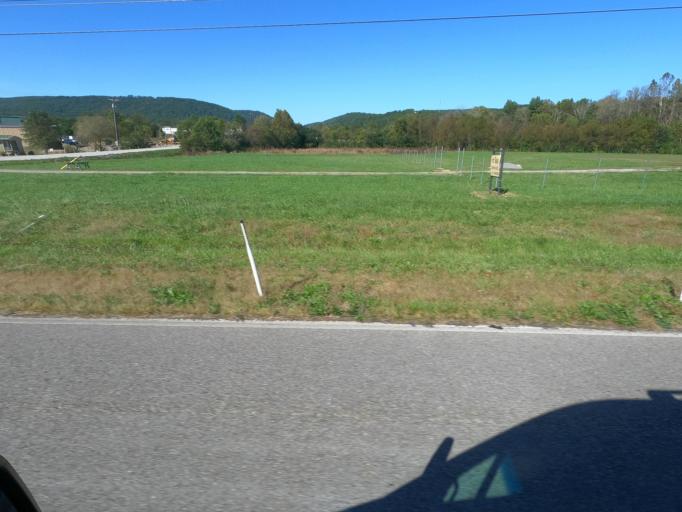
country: US
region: Tennessee
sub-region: Hamilton County
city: Sale Creek
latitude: 35.3453
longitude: -85.1276
